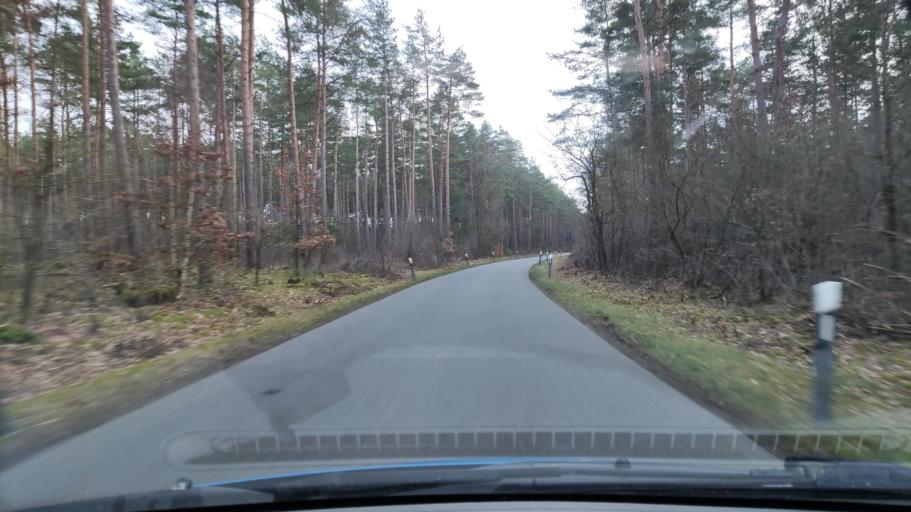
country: DE
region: Lower Saxony
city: Gerdau
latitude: 52.9458
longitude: 10.4296
